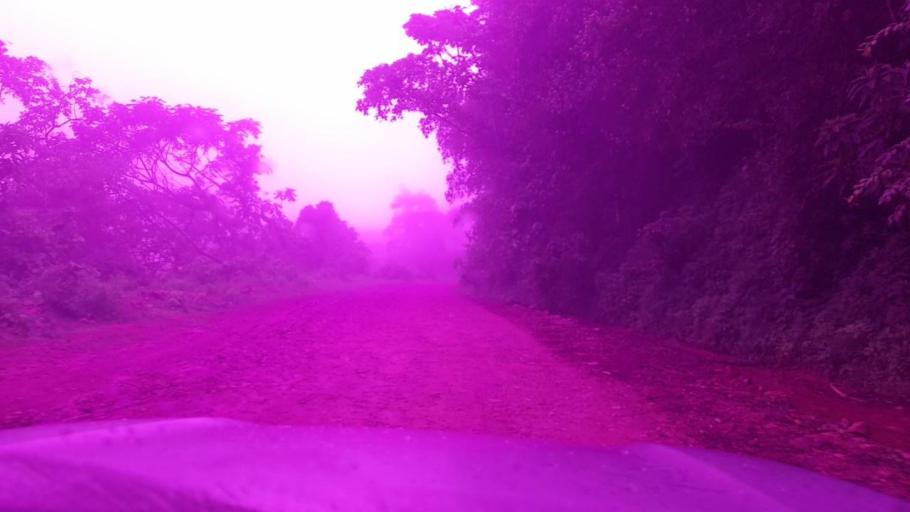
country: ET
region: Southern Nations, Nationalities, and People's Region
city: Bonga
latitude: 7.5153
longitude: 36.0579
